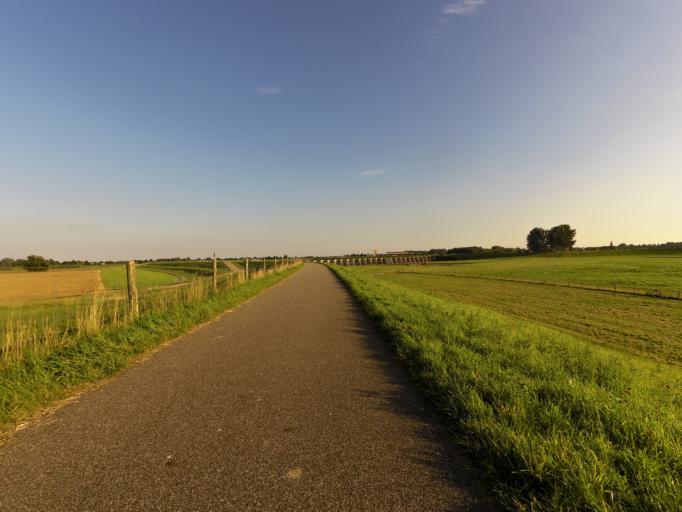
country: NL
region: Gelderland
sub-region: Gemeente Westervoort
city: Westervoort
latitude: 51.9544
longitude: 5.9552
